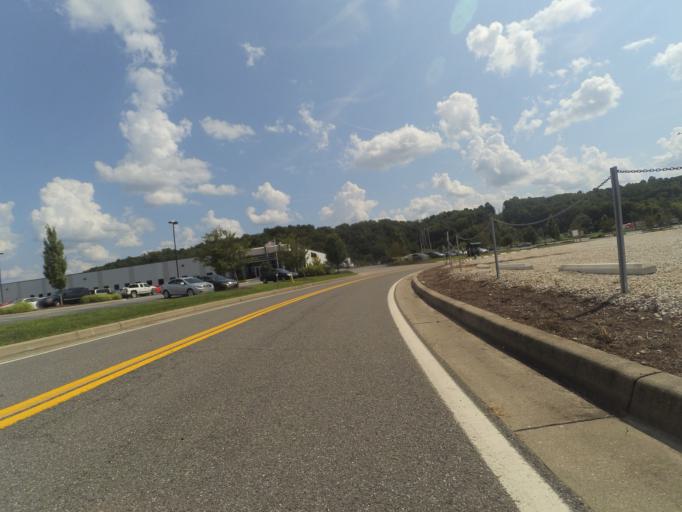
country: US
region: West Virginia
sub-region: Cabell County
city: Huntington
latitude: 38.3948
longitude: -82.4212
